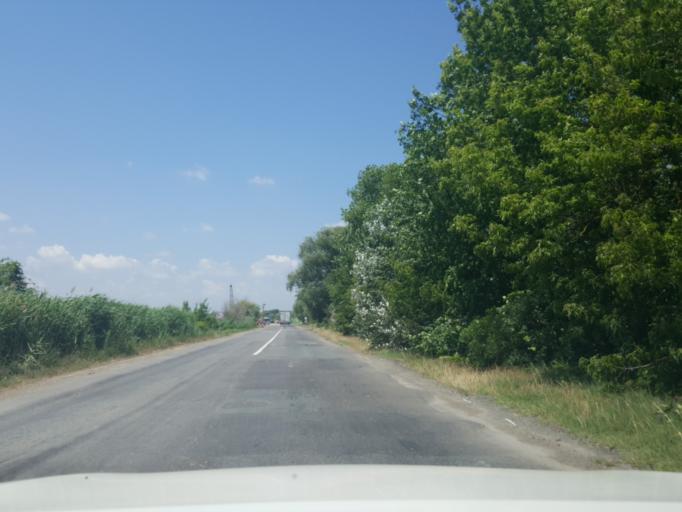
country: UA
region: Odessa
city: Bilyayivka
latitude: 46.4134
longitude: 30.1614
